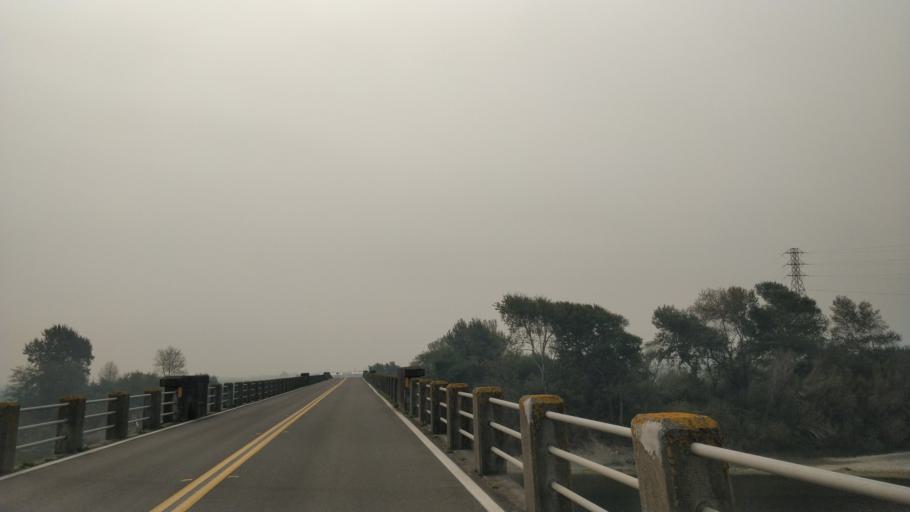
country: US
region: California
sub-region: Humboldt County
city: Fortuna
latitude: 40.6124
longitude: -124.2040
